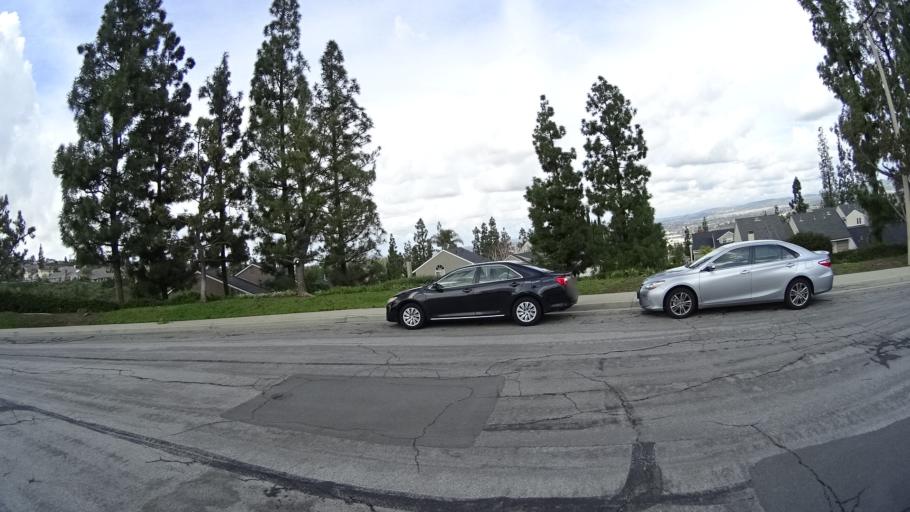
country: US
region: California
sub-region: Orange County
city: Villa Park
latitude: 33.8424
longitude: -117.7804
